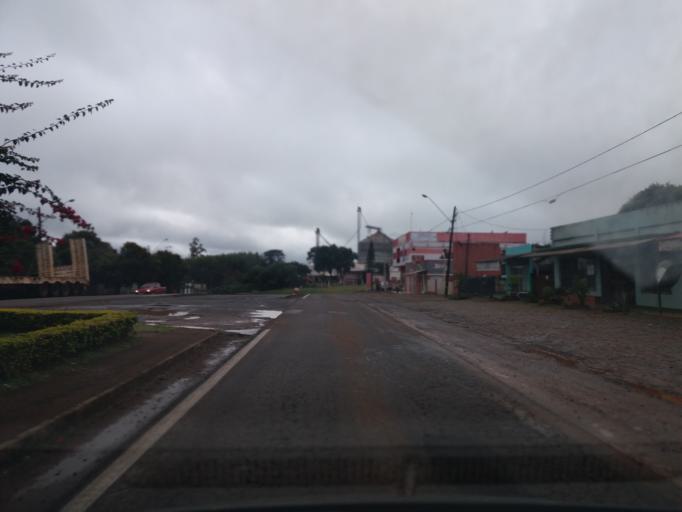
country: BR
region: Parana
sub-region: Cascavel
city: Cascavel
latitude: -25.2801
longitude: -53.5673
